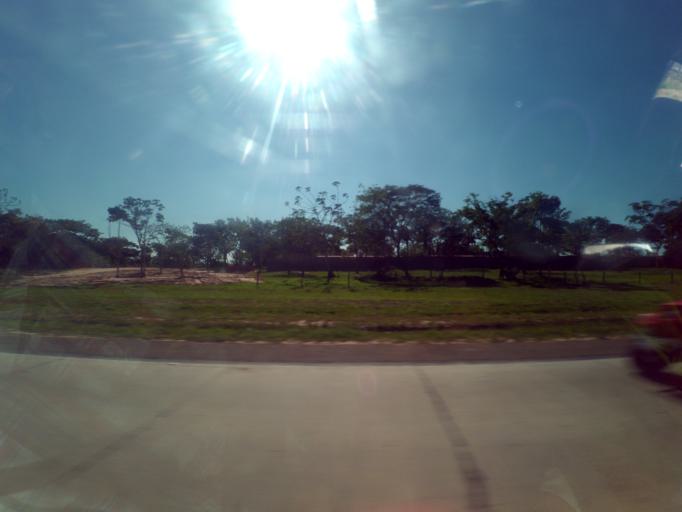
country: BO
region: Santa Cruz
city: Santa Cruz de la Sierra
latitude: -17.7797
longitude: -63.2484
